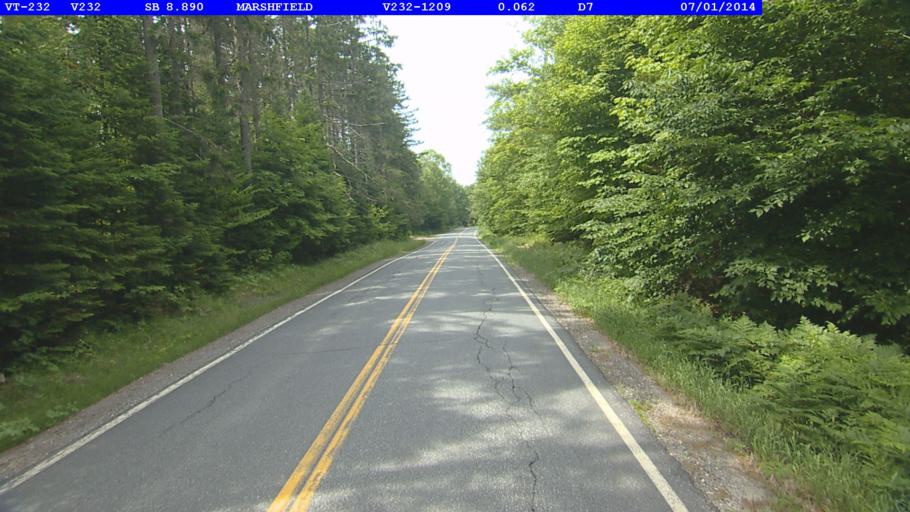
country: US
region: Vermont
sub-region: Caledonia County
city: Hardwick
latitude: 44.3182
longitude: -72.2949
